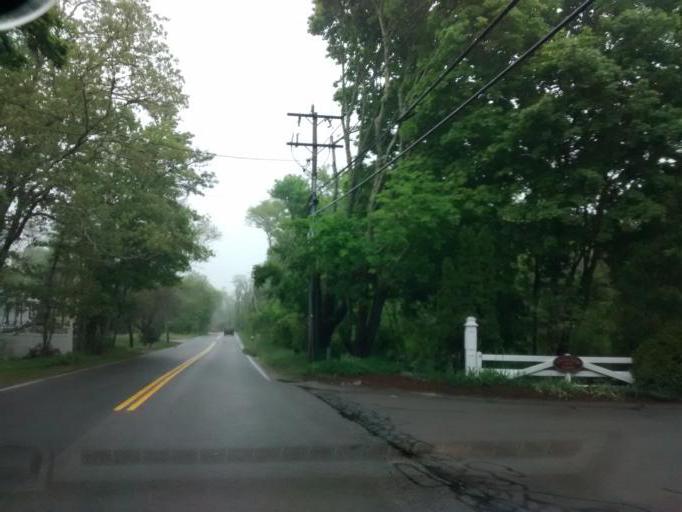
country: US
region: Massachusetts
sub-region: Barnstable County
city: Monument Beach
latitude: 41.7220
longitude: -70.6041
